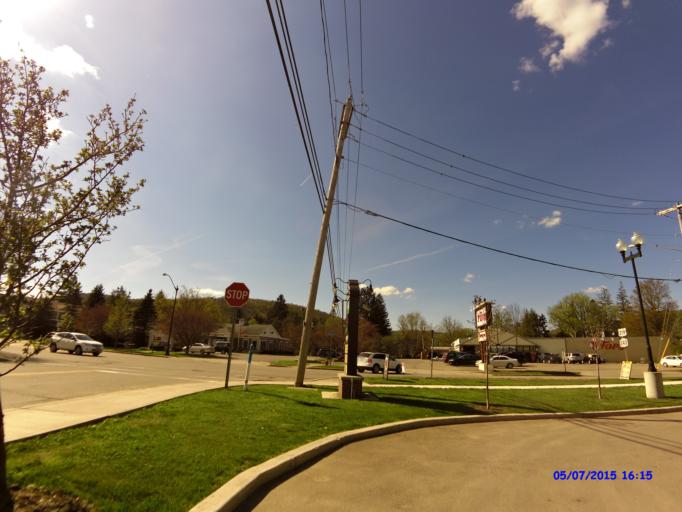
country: US
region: New York
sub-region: Cattaraugus County
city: Salamanca
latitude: 42.2764
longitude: -78.6692
